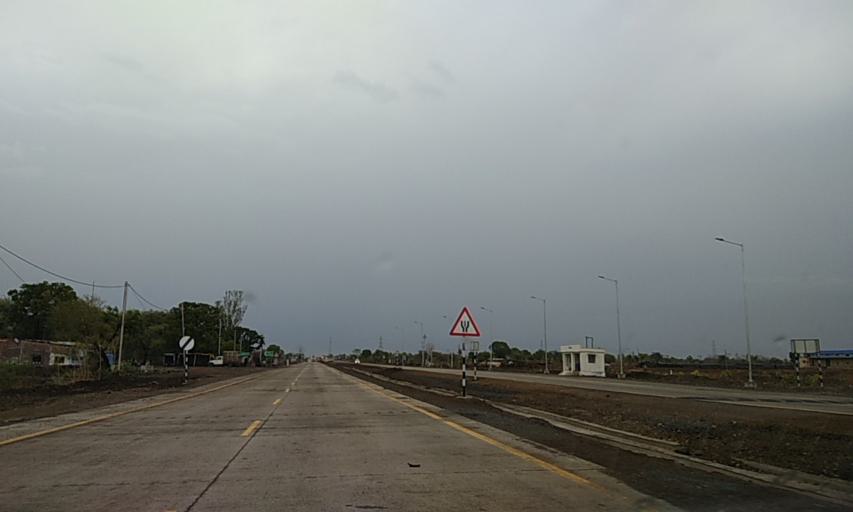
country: IN
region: Madhya Pradesh
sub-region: Rajgarh
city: Sarangpur
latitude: 23.6284
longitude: 76.5695
